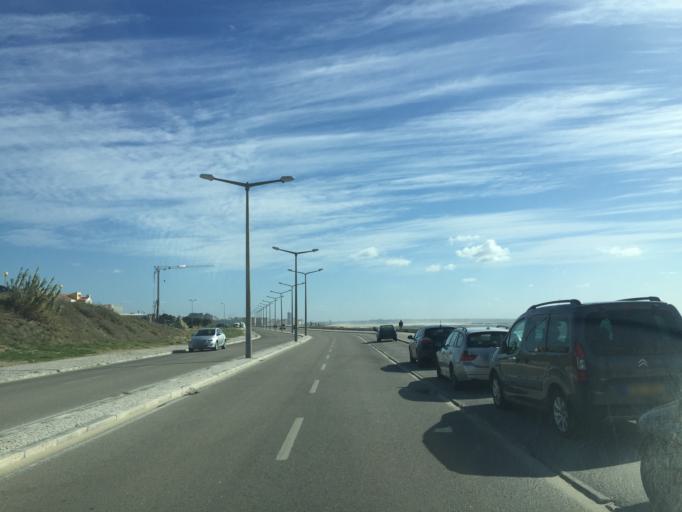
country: PT
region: Coimbra
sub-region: Figueira da Foz
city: Buarcos
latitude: 40.1692
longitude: -8.8879
